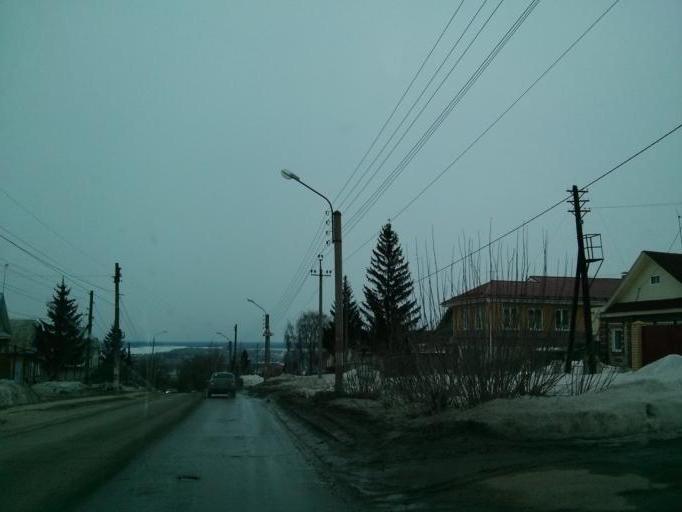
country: RU
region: Nizjnij Novgorod
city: Afonino
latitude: 56.2963
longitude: 44.0868
